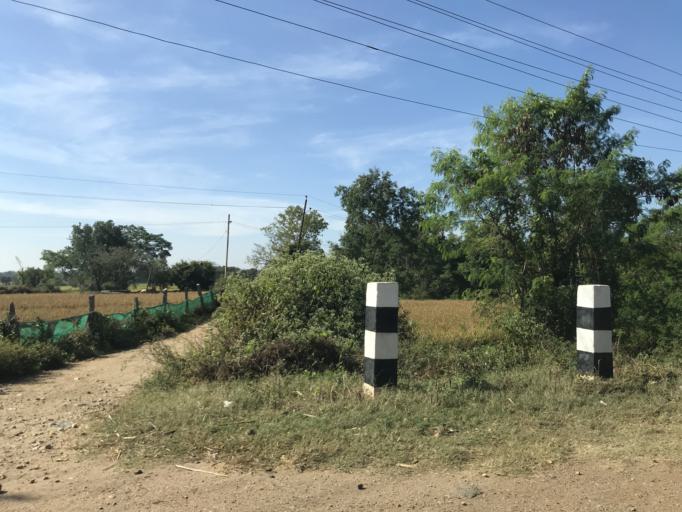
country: IN
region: Karnataka
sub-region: Mysore
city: Heggadadevankote
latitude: 12.1258
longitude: 76.4547
